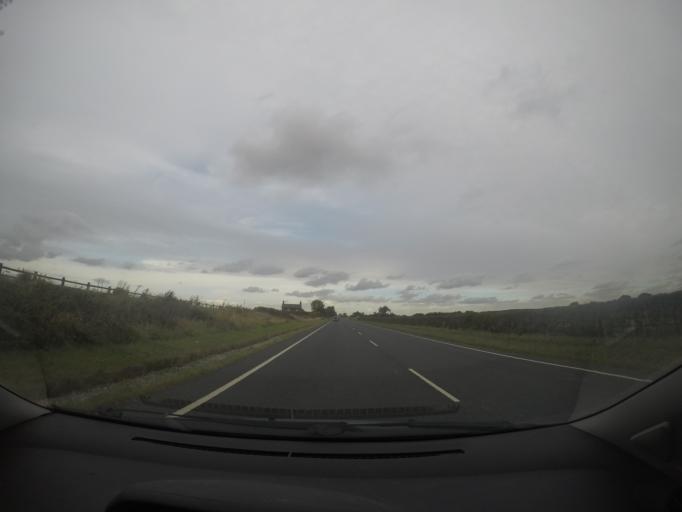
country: GB
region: England
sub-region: North Yorkshire
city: Barlby
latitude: 53.8126
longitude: -1.0407
